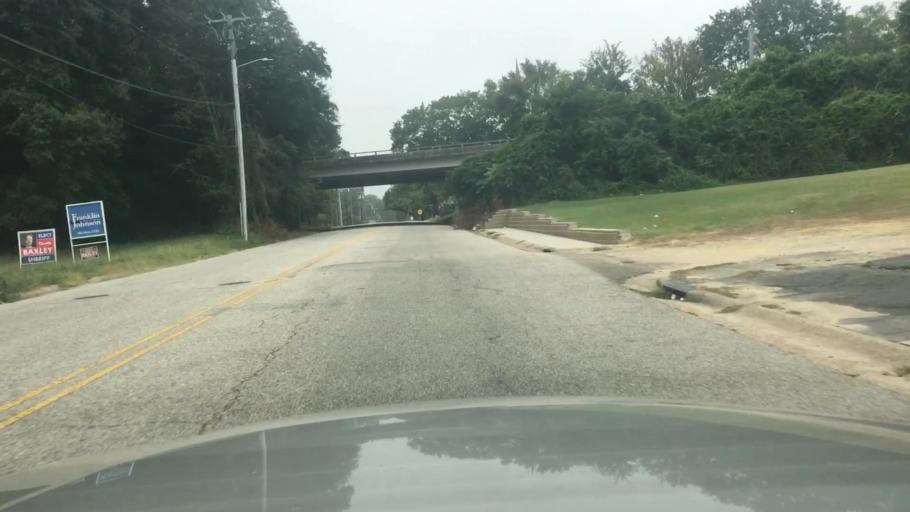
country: US
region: North Carolina
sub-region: Cumberland County
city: Fayetteville
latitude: 35.0664
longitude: -78.8854
